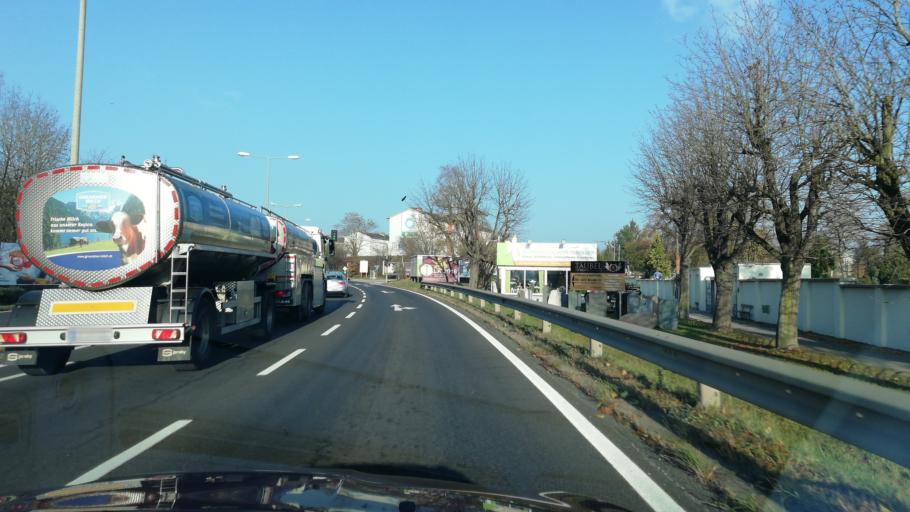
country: AT
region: Upper Austria
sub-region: Wels Stadt
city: Wels
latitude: 48.1734
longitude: 14.0310
